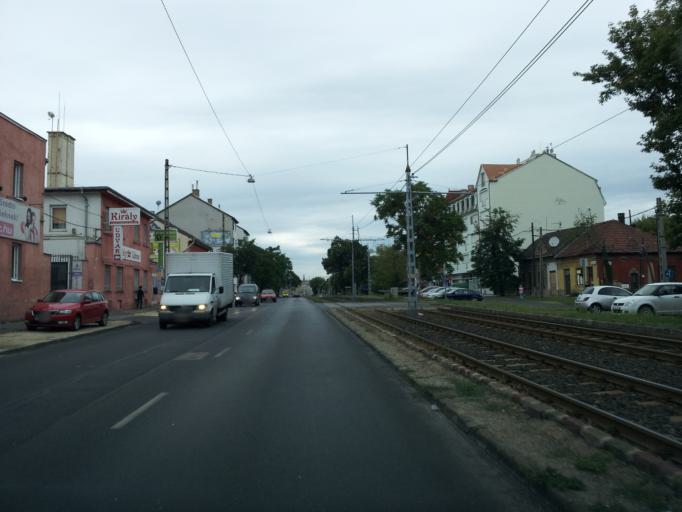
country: HU
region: Budapest
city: Budapest XIV. keruelet
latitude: 47.5155
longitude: 19.1189
